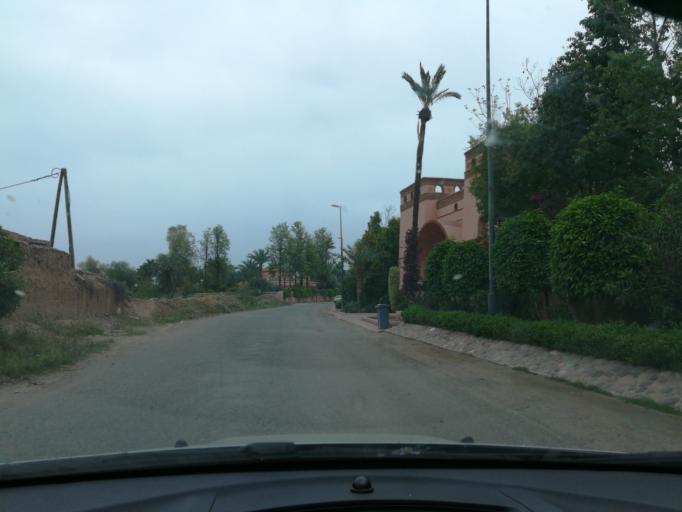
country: MA
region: Marrakech-Tensift-Al Haouz
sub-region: Marrakech
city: Marrakesh
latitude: 31.6555
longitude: -7.9809
